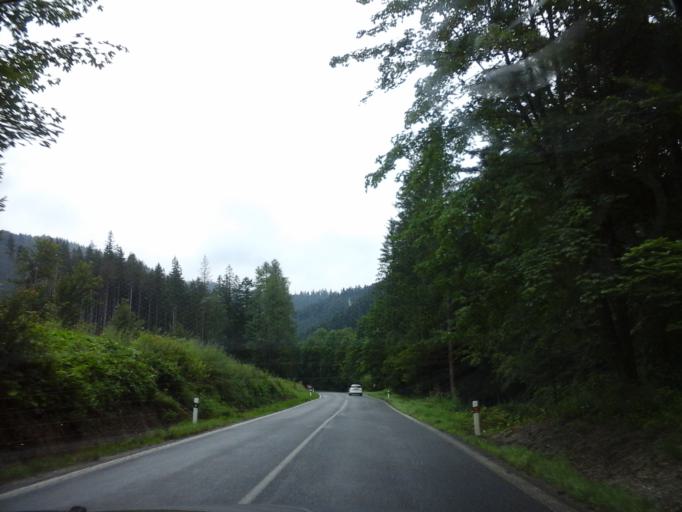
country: SK
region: Presovsky
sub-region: Okres Poprad
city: Zdiar
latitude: 49.2452
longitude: 20.3095
